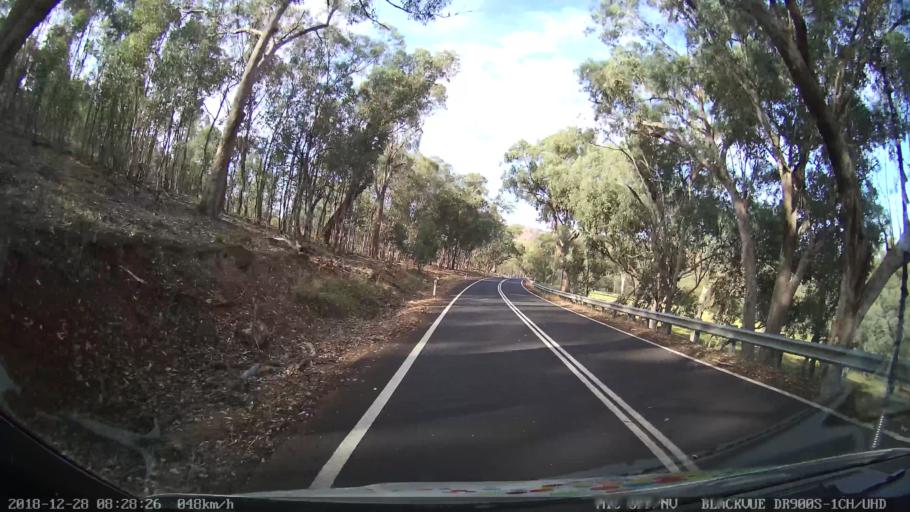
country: AU
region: New South Wales
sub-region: Blayney
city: Blayney
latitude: -33.9416
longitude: 149.3276
